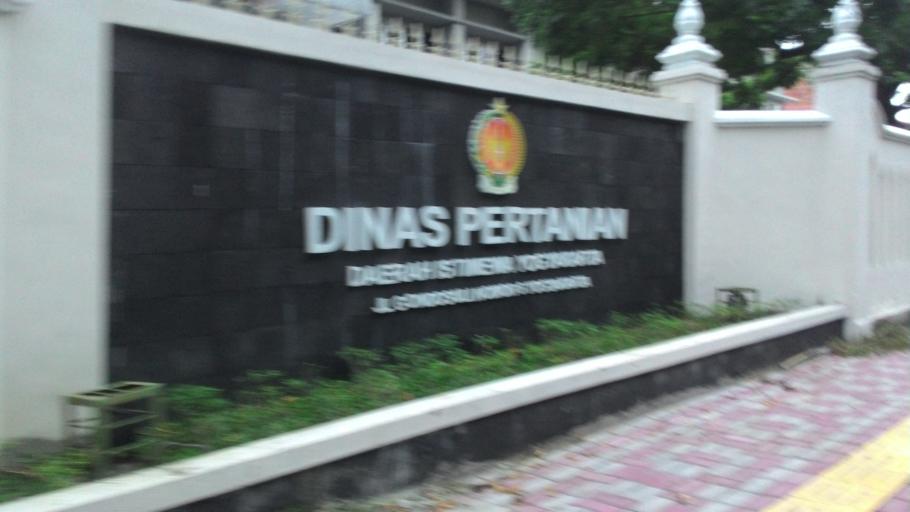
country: ID
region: Daerah Istimewa Yogyakarta
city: Yogyakarta
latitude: -7.7965
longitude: 110.3851
